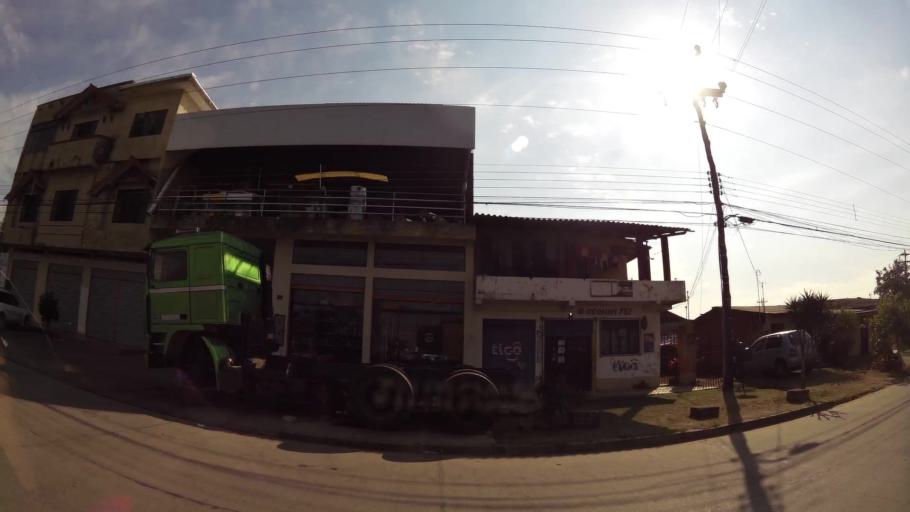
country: BO
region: Santa Cruz
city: Santa Cruz de la Sierra
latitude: -17.7357
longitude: -63.1581
